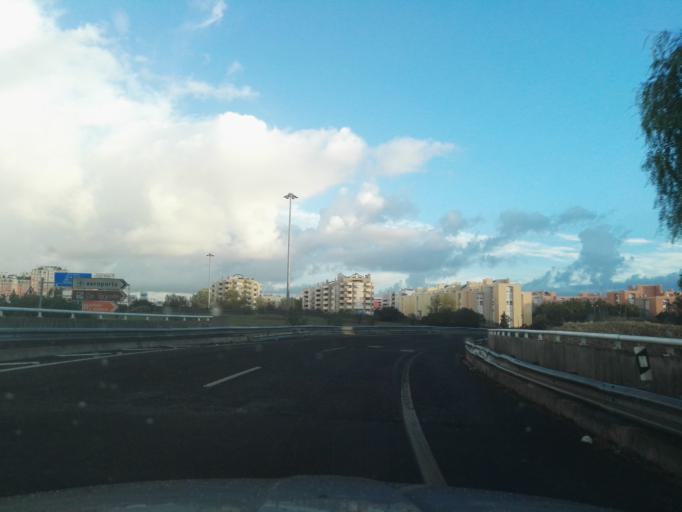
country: PT
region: Lisbon
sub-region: Odivelas
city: Pontinha
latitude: 38.7559
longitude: -9.1716
